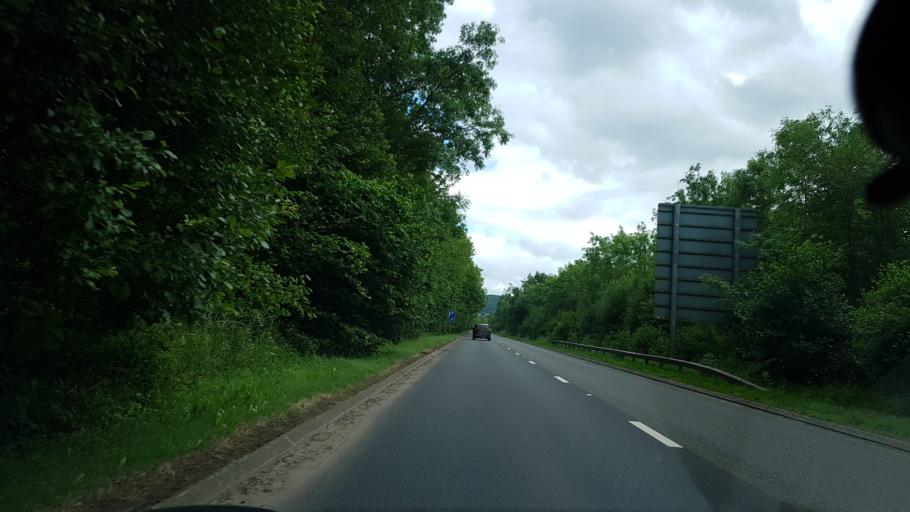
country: GB
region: Wales
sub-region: Monmouthshire
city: Abergavenny
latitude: 51.8479
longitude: -3.0008
